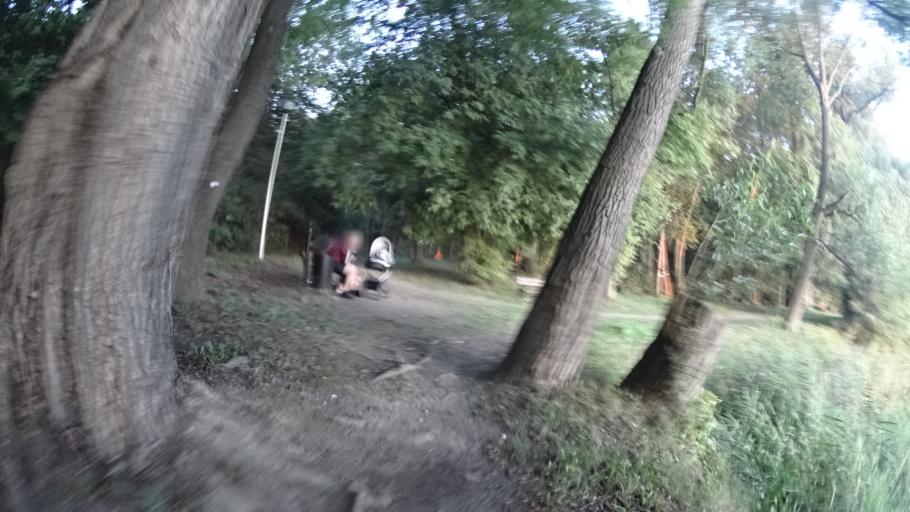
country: PL
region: Masovian Voivodeship
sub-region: Powiat warszawski zachodni
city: Ozarow Mazowiecki
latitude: 52.2182
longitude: 20.7745
